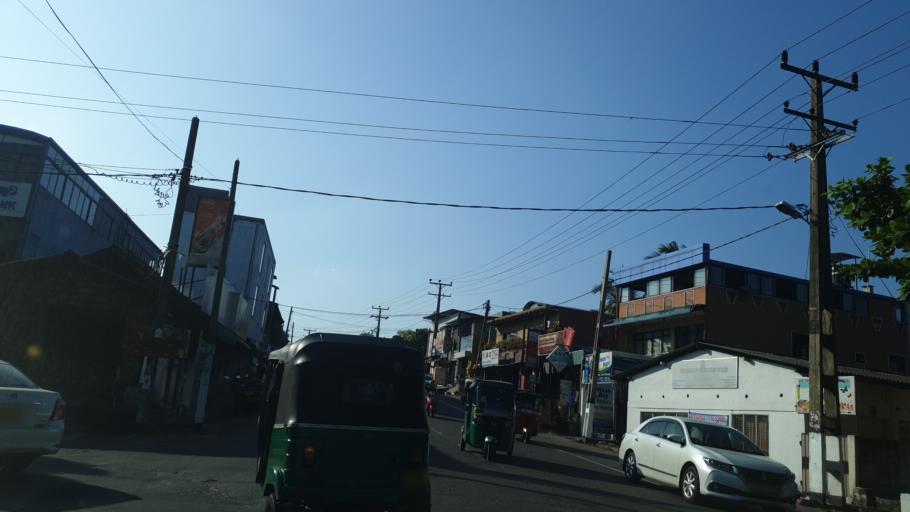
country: LK
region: Western
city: Sri Jayewardenepura Kotte
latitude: 6.8788
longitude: 79.9220
